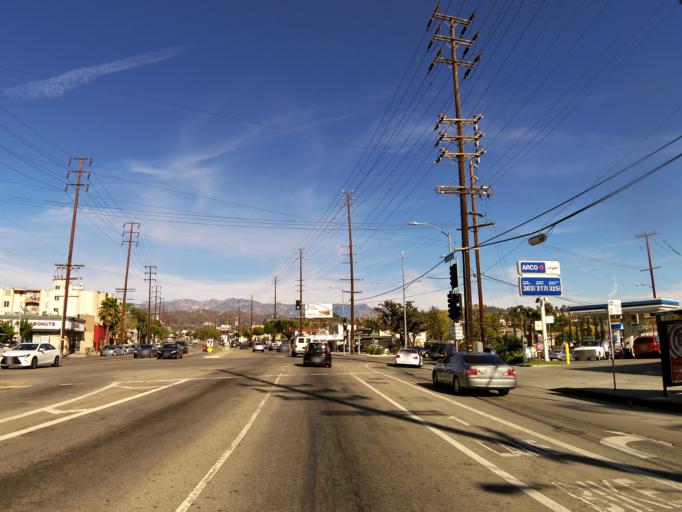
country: US
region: California
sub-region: Los Angeles County
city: Glendale
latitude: 34.1238
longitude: -118.2211
